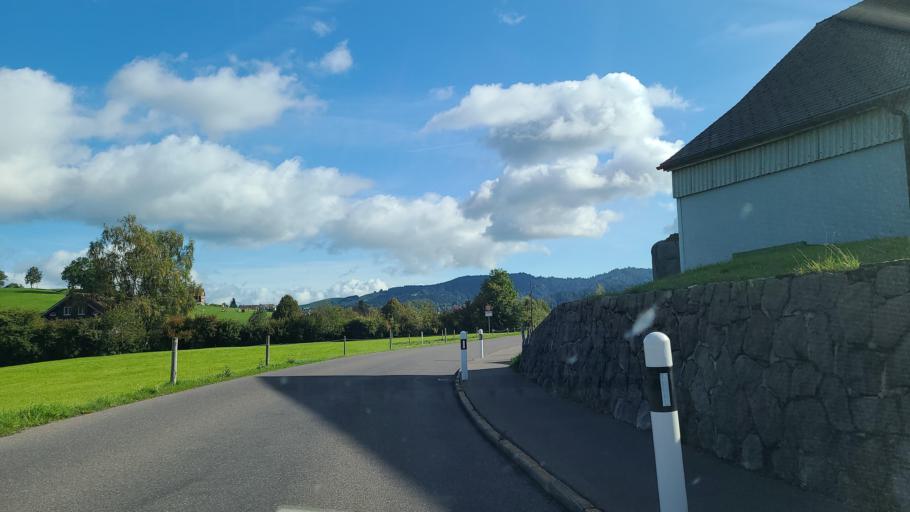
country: CH
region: Schwyz
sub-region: Bezirk Einsiedeln
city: Einsiedeln
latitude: 47.1388
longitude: 8.7544
